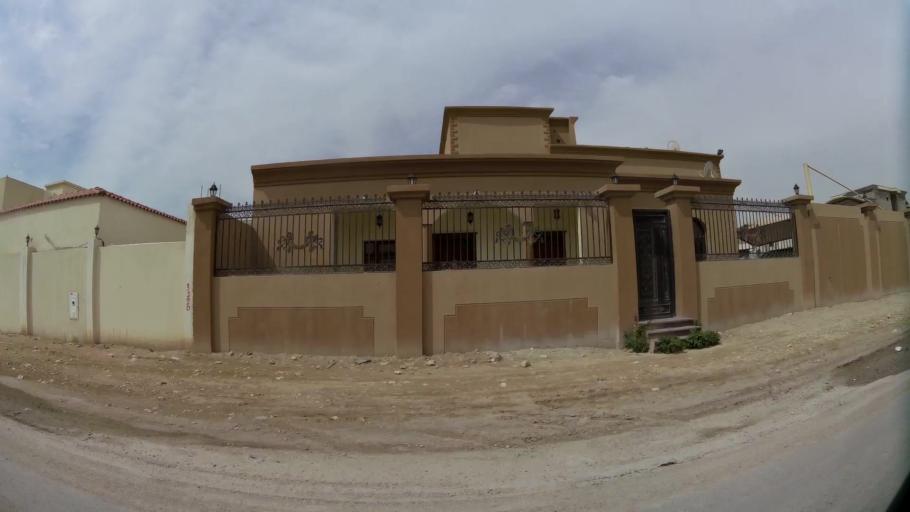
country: QA
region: Baladiyat ar Rayyan
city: Ar Rayyan
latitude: 25.2137
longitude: 51.4583
